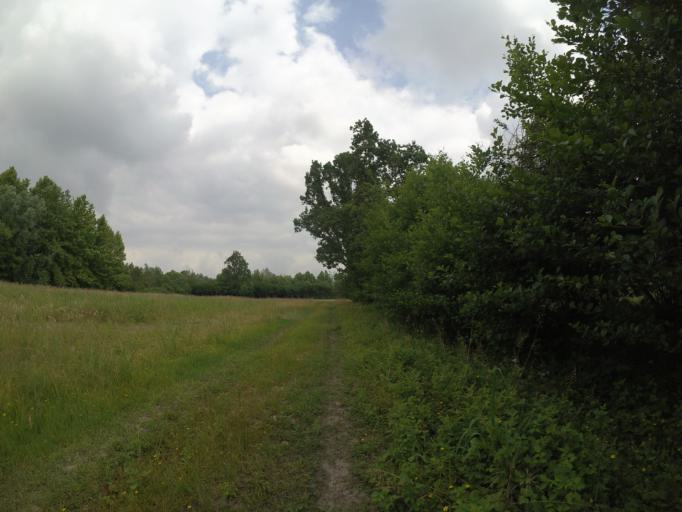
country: IT
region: Friuli Venezia Giulia
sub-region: Provincia di Udine
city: Bertiolo
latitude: 45.9208
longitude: 13.0330
